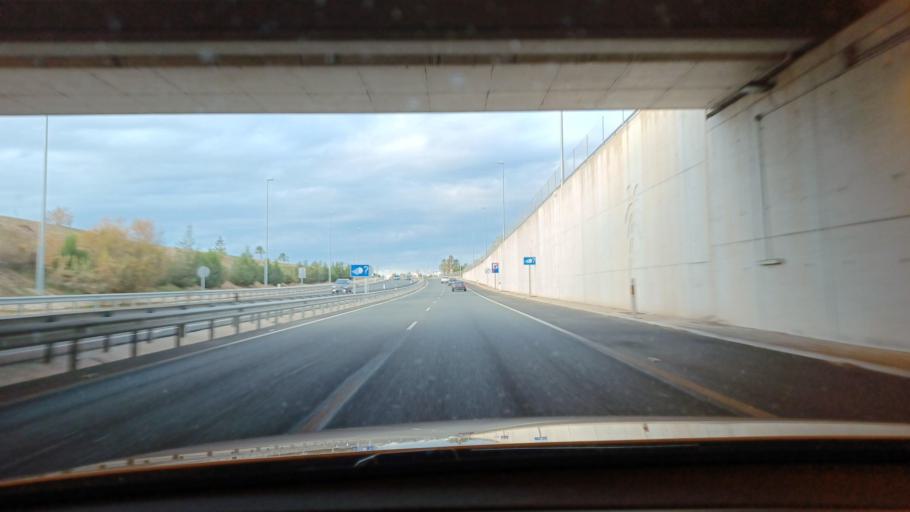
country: ES
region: Valencia
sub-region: Provincia de Alicante
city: Elche
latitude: 38.2579
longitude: -0.6815
